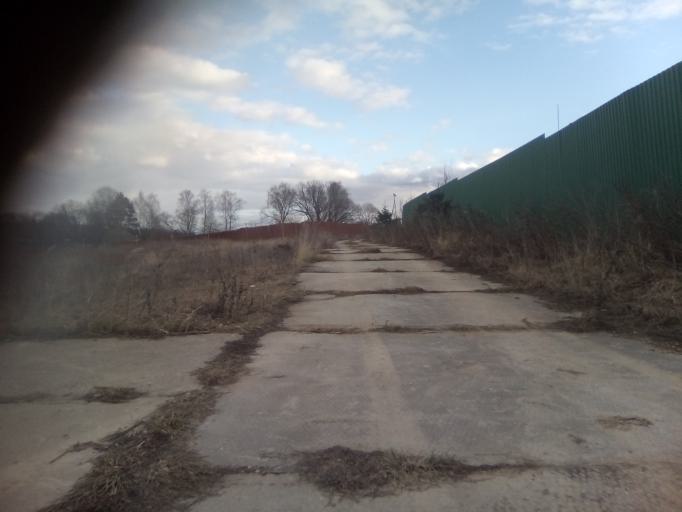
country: RU
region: Moskovskaya
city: Filimonki
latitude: 55.5780
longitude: 37.3377
